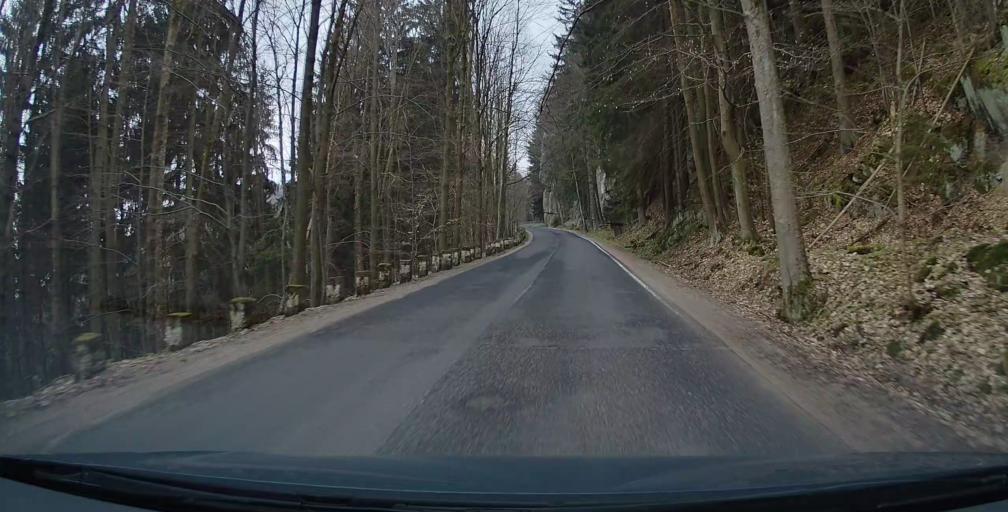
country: PL
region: Lower Silesian Voivodeship
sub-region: Powiat klodzki
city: Radkow
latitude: 50.4802
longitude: 16.3864
